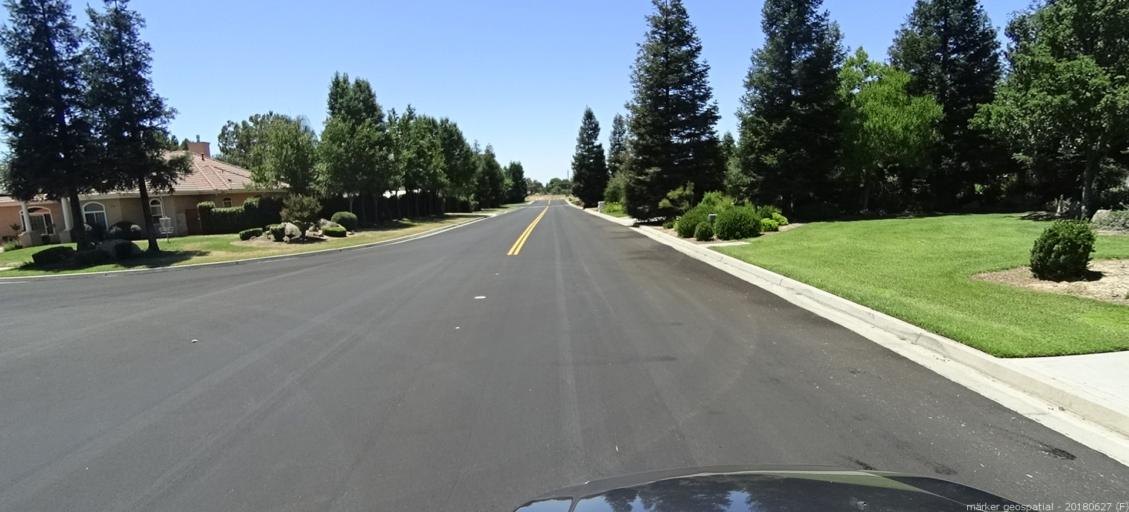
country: US
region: California
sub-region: Madera County
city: Bonadelle Ranchos-Madera Ranchos
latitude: 36.9332
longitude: -119.9098
